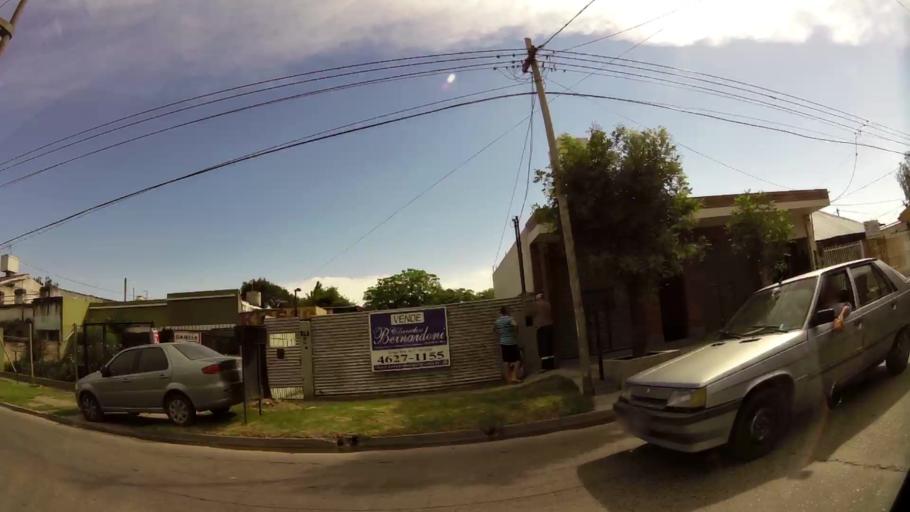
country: AR
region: Buenos Aires
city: Ituzaingo
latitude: -34.6432
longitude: -58.6934
